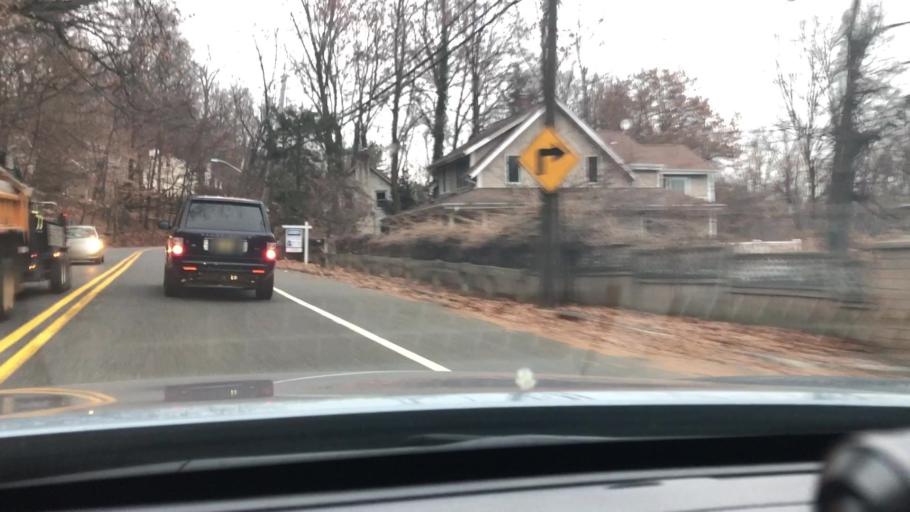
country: US
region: New Jersey
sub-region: Bergen County
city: Woodcliff Lake
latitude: 41.0011
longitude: -74.0752
